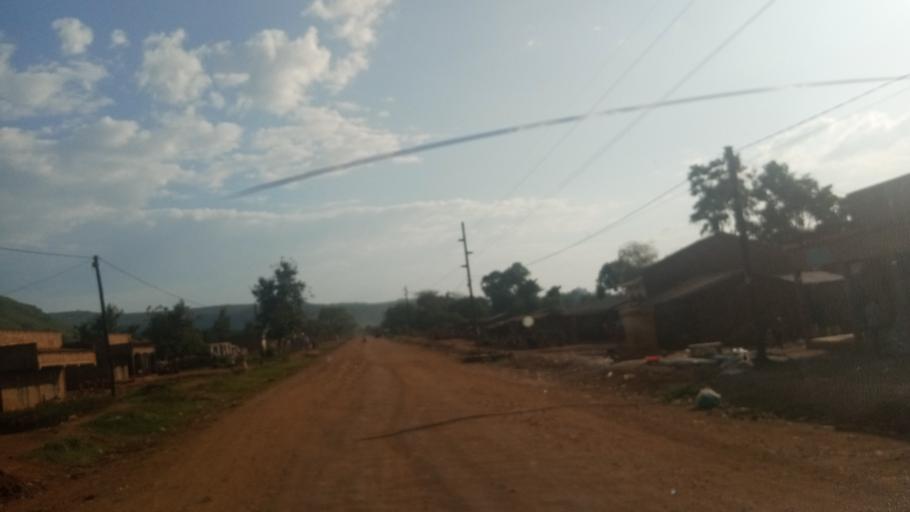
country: UG
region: Eastern Region
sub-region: Kapchorwa District
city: Kapchorwa
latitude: 1.4180
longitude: 34.3510
